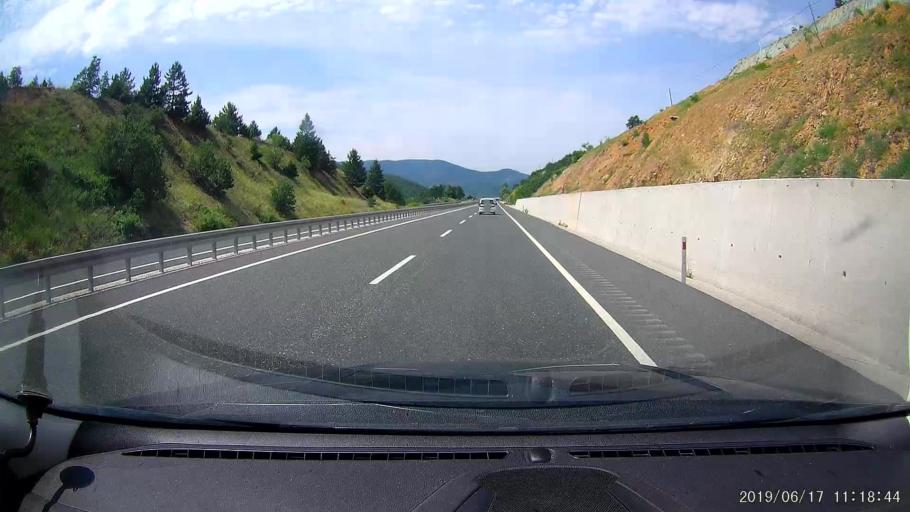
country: TR
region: Cankiri
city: Yaprakli
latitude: 40.9311
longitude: 33.8439
